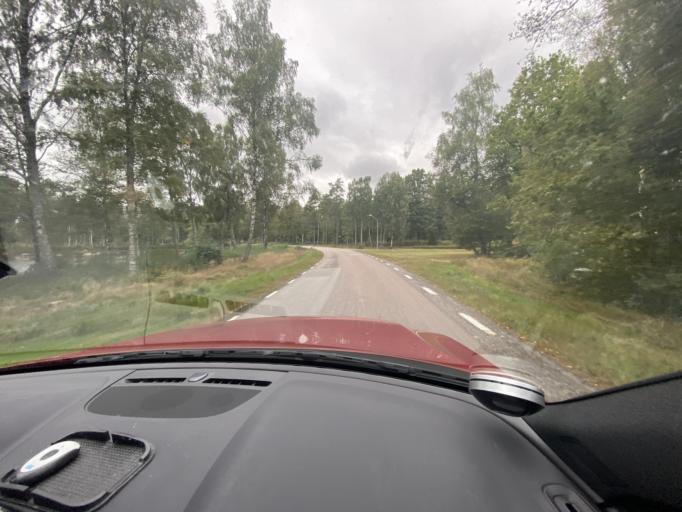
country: SE
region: Kronoberg
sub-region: Markaryds Kommun
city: Markaryd
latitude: 56.5031
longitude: 13.5518
